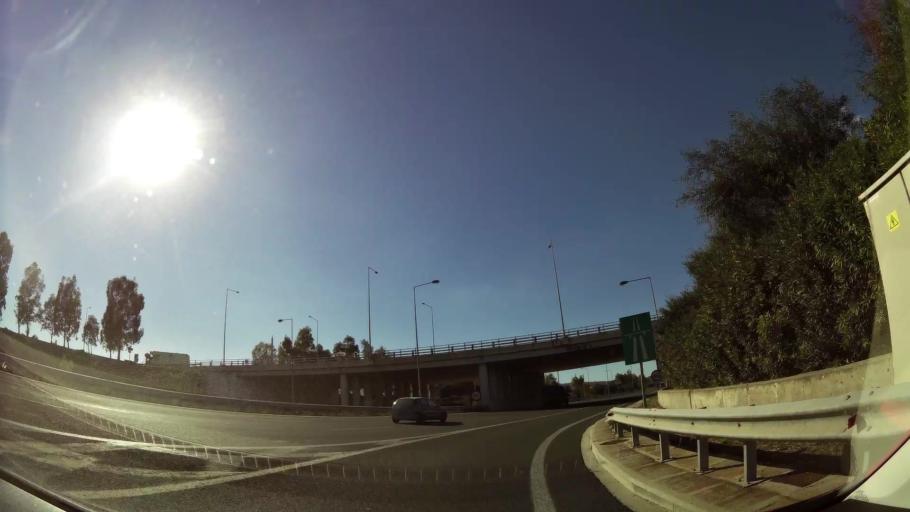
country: GR
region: Attica
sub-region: Nomarchia Anatolikis Attikis
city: Pallini
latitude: 37.9926
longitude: 23.8914
